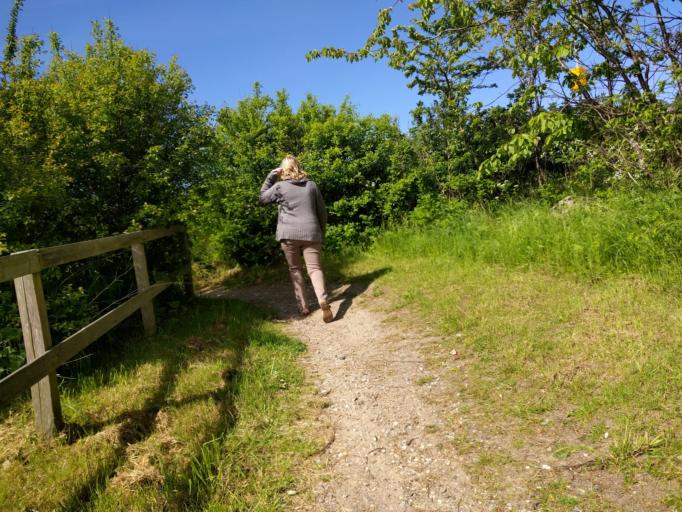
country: DK
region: Zealand
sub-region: Guldborgsund Kommune
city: Stubbekobing
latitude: 54.9135
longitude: 12.0517
